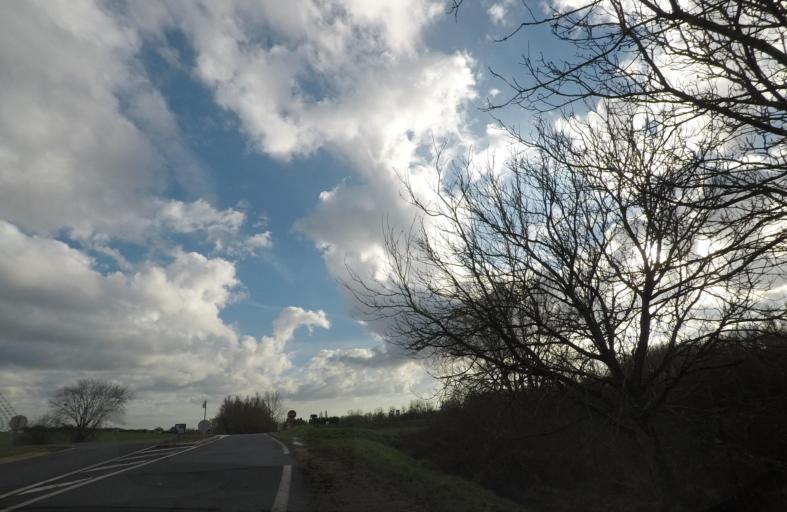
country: FR
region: Centre
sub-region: Departement du Cher
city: Bourges
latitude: 47.0463
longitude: 2.4202
